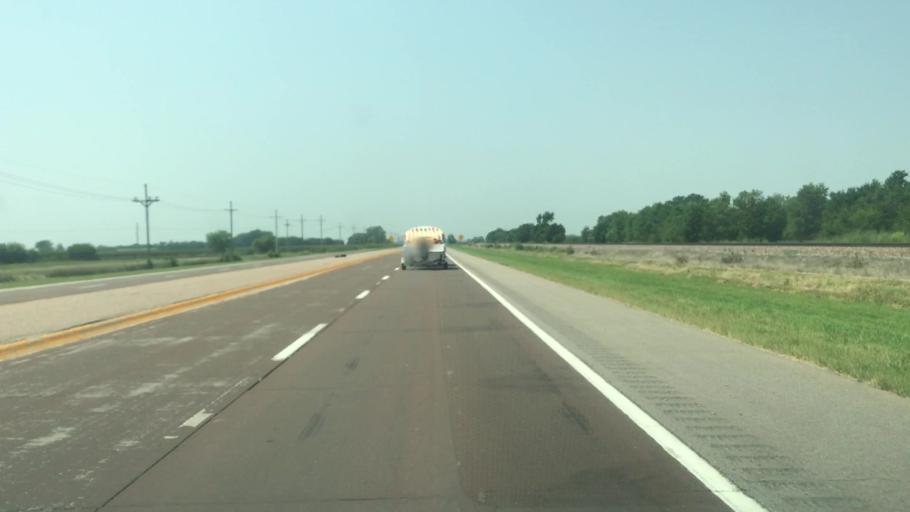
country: US
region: Nebraska
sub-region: Hall County
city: Grand Island
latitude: 40.9580
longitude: -98.4044
